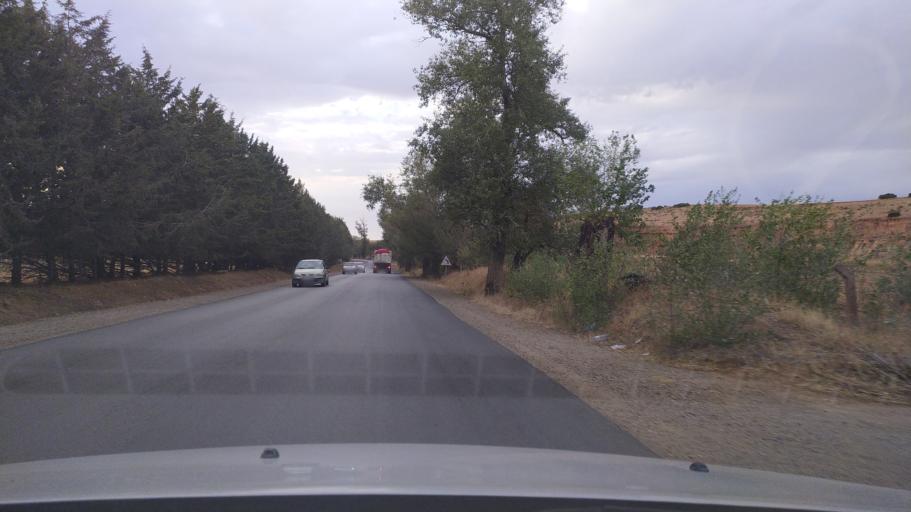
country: DZ
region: Tiaret
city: Frenda
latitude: 35.0470
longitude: 1.0823
